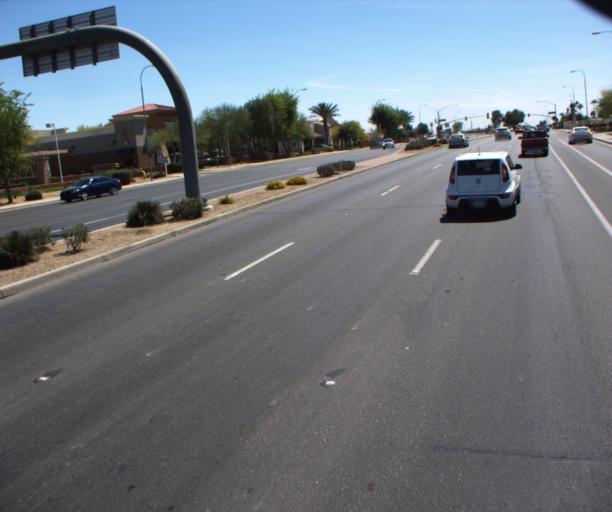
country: US
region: Arizona
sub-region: Maricopa County
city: Chandler
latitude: 33.2860
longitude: -111.8416
